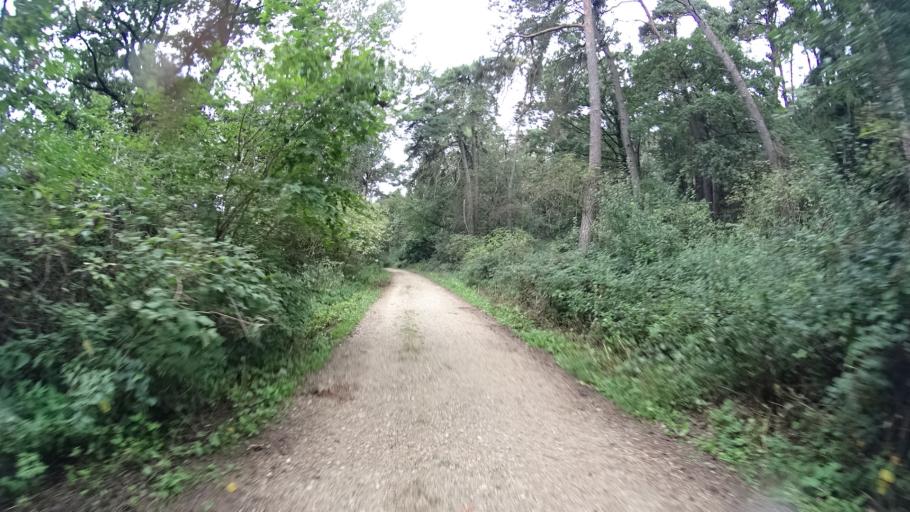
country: DE
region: Bavaria
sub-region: Upper Bavaria
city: Bohmfeld
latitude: 48.8463
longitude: 11.3555
